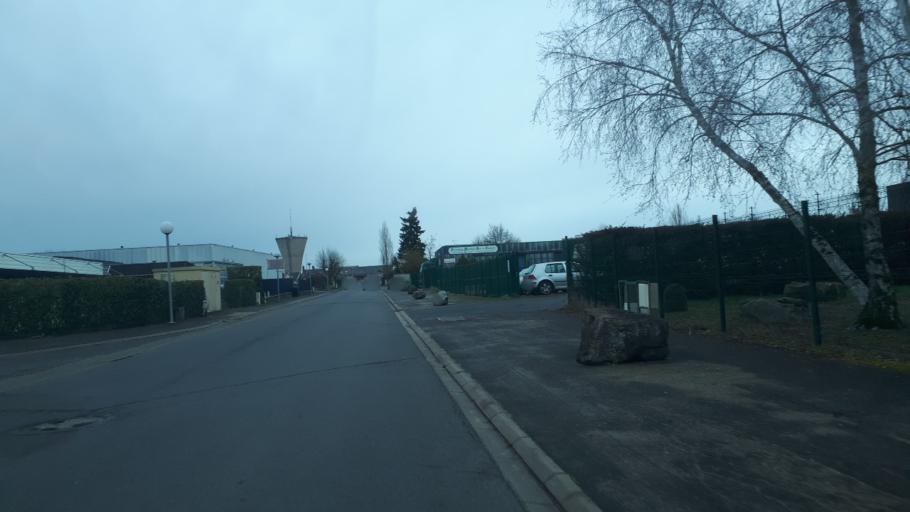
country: FR
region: Centre
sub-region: Departement du Loir-et-Cher
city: Romorantin-Lanthenay
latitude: 47.3401
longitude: 1.7457
